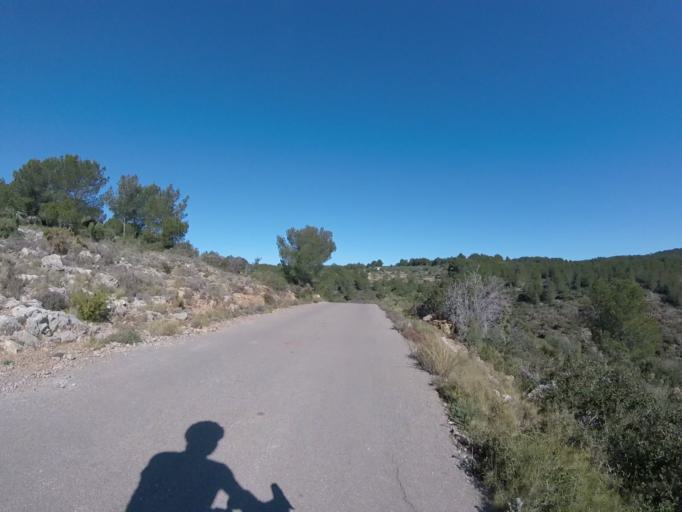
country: ES
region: Valencia
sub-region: Provincia de Castello
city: Benicassim
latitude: 40.0795
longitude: 0.0899
